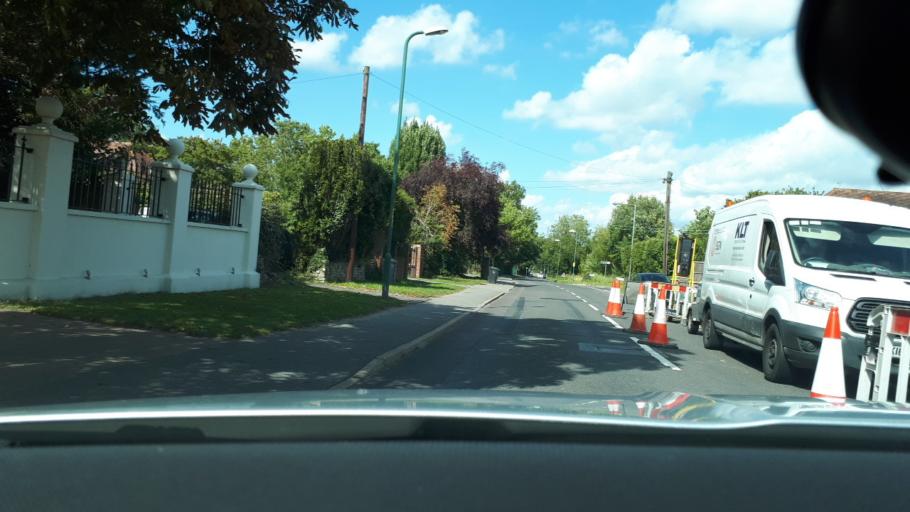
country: GB
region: England
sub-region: Kent
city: Swanley
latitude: 51.4273
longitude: 0.1803
